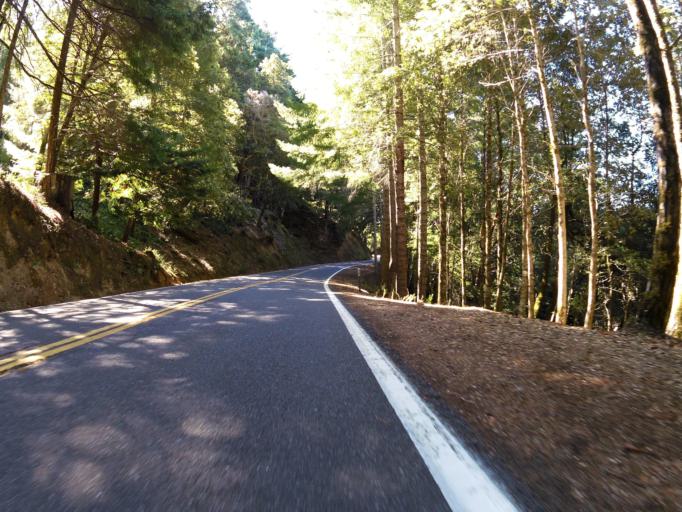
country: US
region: California
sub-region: Humboldt County
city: Redway
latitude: 39.8250
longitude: -123.7794
